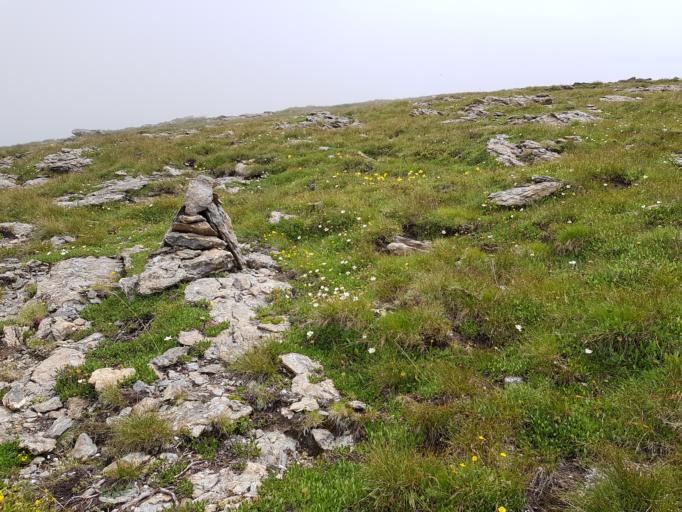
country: IT
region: Piedmont
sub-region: Provincia di Cuneo
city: Frabosa Soprana
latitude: 44.1875
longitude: 7.7764
